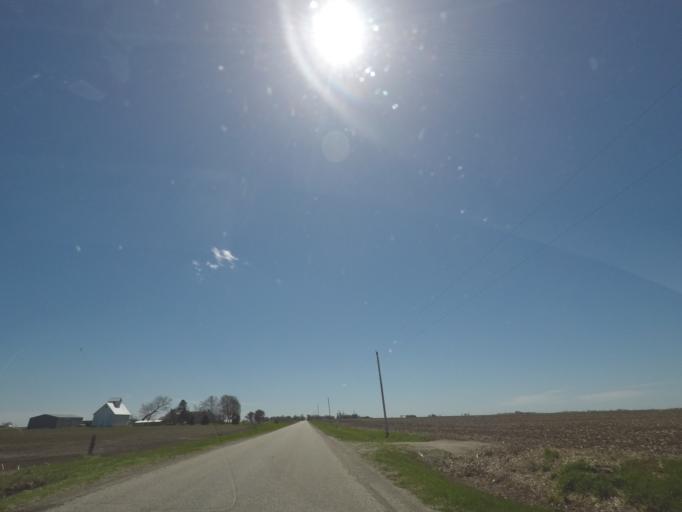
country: US
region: Illinois
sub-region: Logan County
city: Atlanta
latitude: 40.1613
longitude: -89.1936
